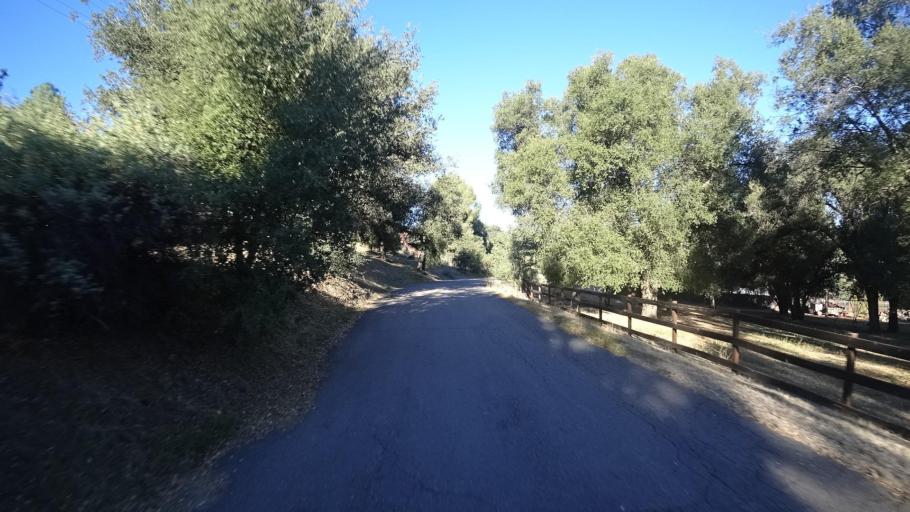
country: US
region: California
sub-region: San Diego County
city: Pine Valley
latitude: 32.8186
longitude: -116.5288
